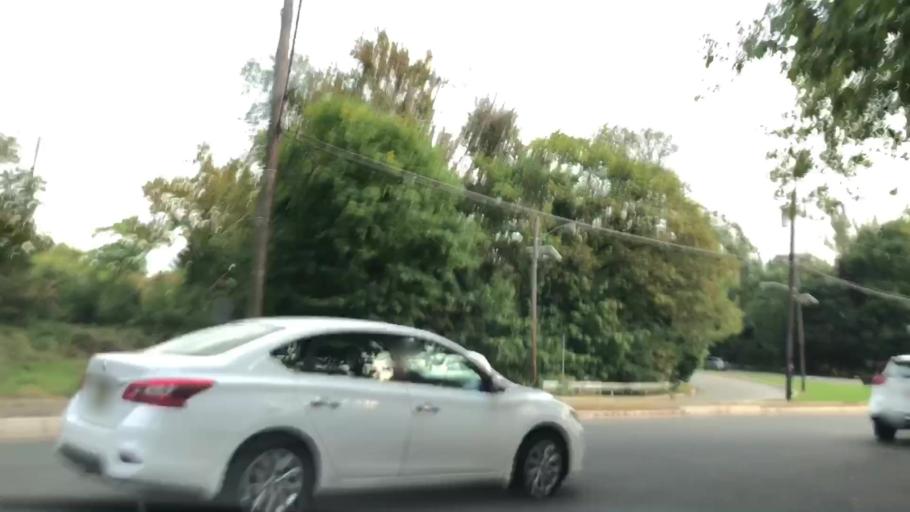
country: US
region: New Jersey
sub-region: Passaic County
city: Little Falls
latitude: 40.8707
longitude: -74.1898
